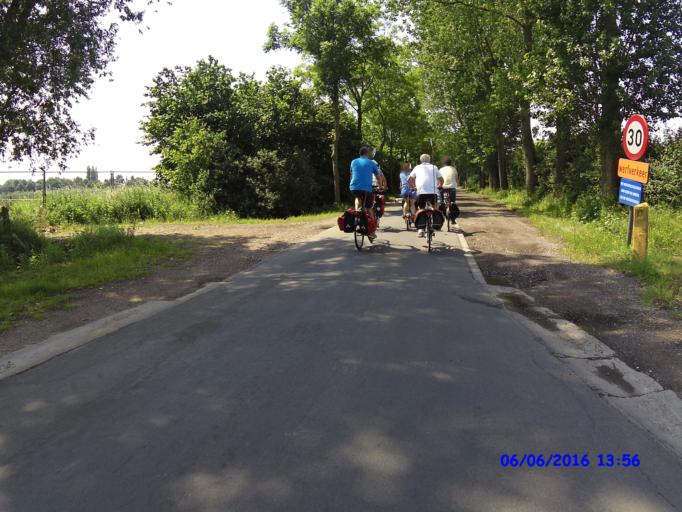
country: BE
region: Flanders
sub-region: Provincie Oost-Vlaanderen
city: Kruibeke
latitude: 51.1930
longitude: 4.3169
